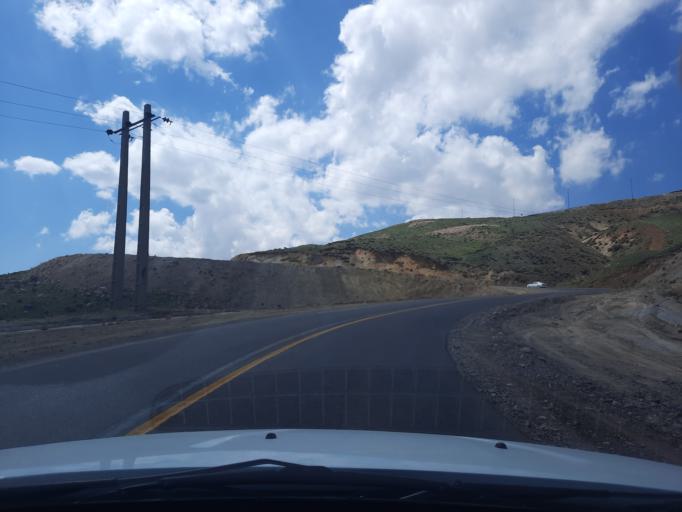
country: IR
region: Qazvin
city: Qazvin
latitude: 36.3816
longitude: 50.2077
